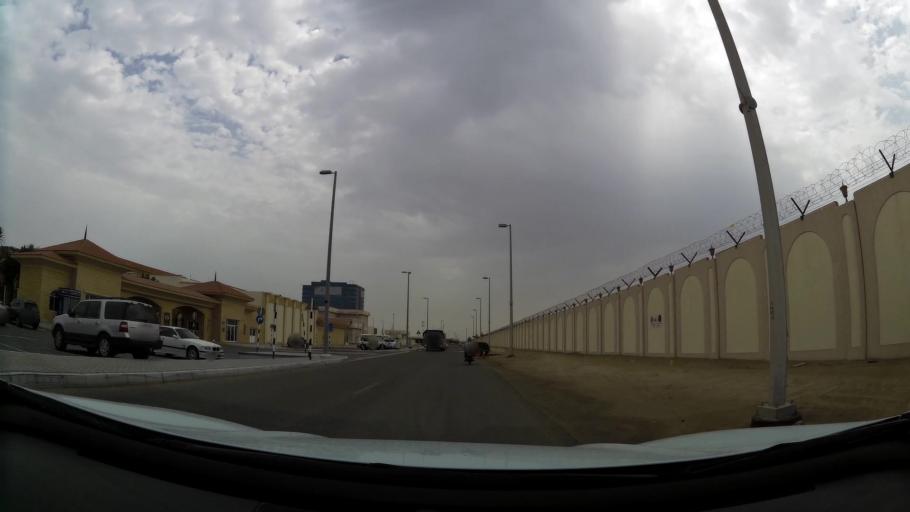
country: AE
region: Abu Dhabi
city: Abu Dhabi
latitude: 24.4292
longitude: 54.4597
